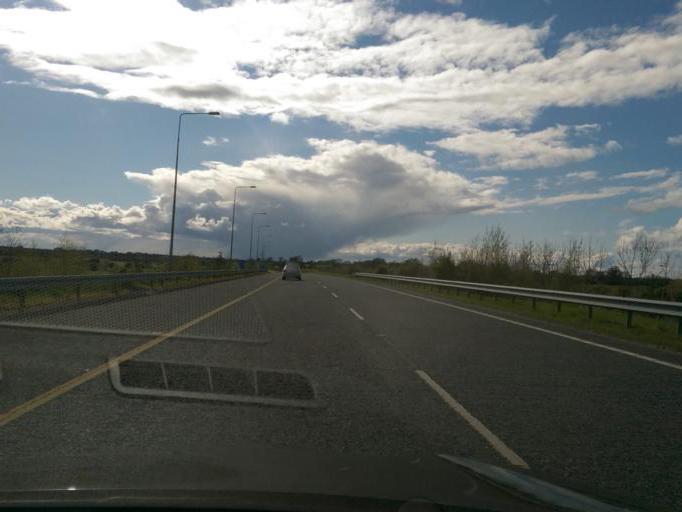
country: IE
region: Leinster
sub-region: An Iarmhi
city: Kinnegad
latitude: 53.4498
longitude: -7.1074
